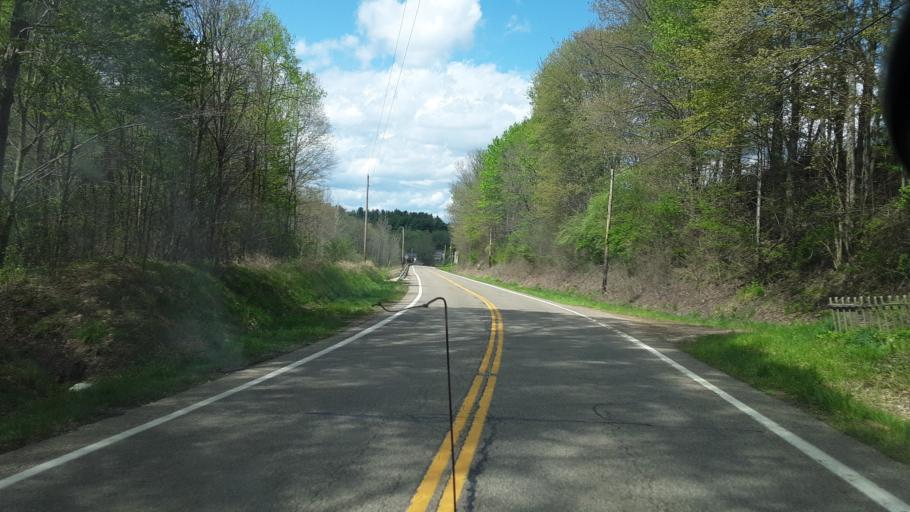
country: US
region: Ohio
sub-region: Coshocton County
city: Coshocton
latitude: 40.2139
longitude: -81.8344
